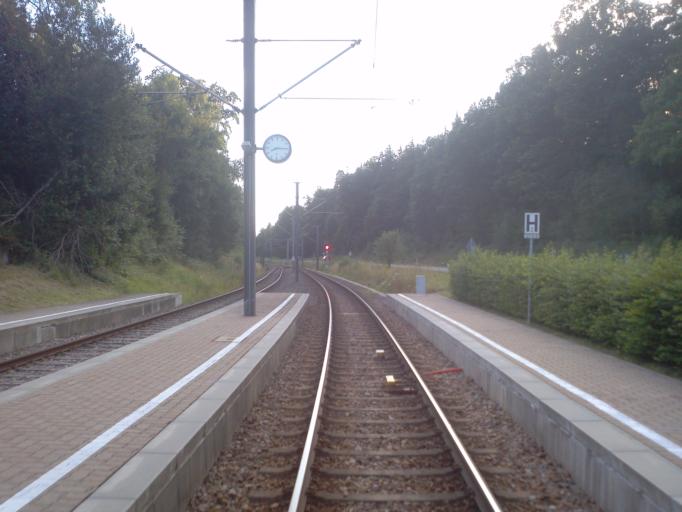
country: DE
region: Baden-Wuerttemberg
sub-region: Karlsruhe Region
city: Dobel
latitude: 48.8848
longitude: 8.5082
